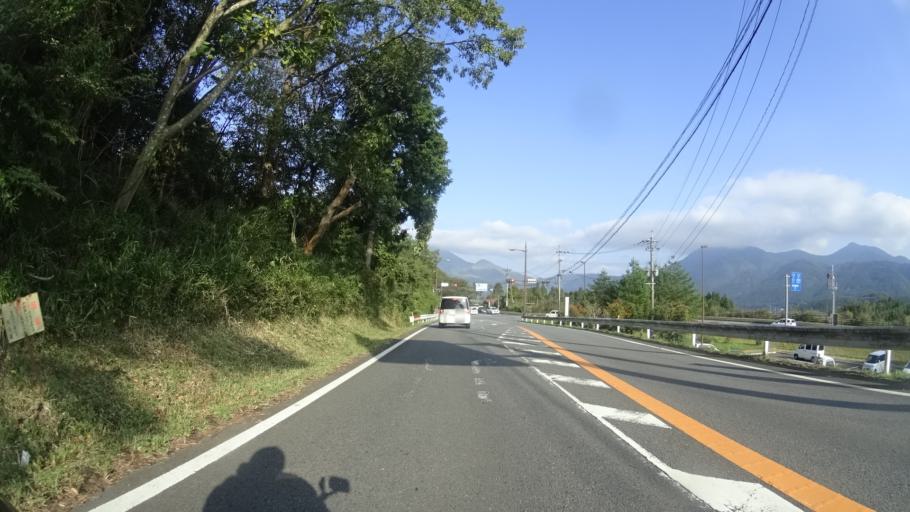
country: JP
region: Oita
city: Beppu
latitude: 33.2612
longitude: 131.3284
